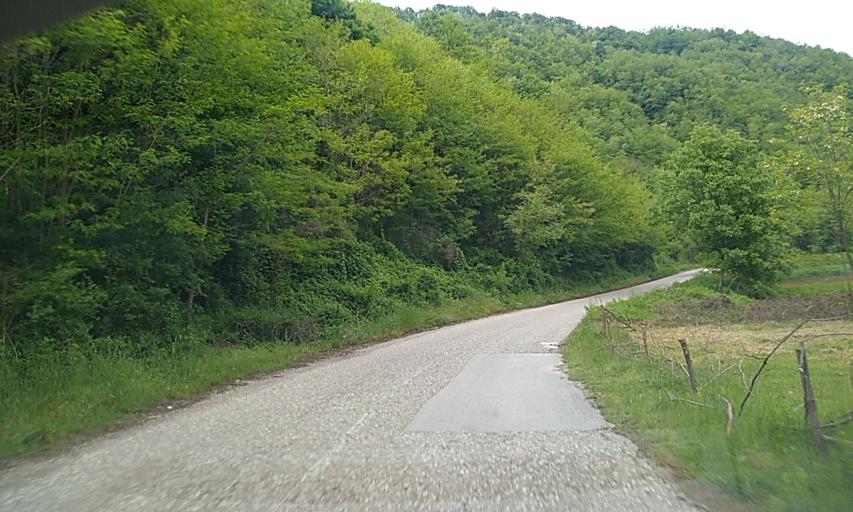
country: RS
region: Central Serbia
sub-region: Pcinjski Okrug
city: Vladicin Han
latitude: 42.7526
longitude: 22.0609
